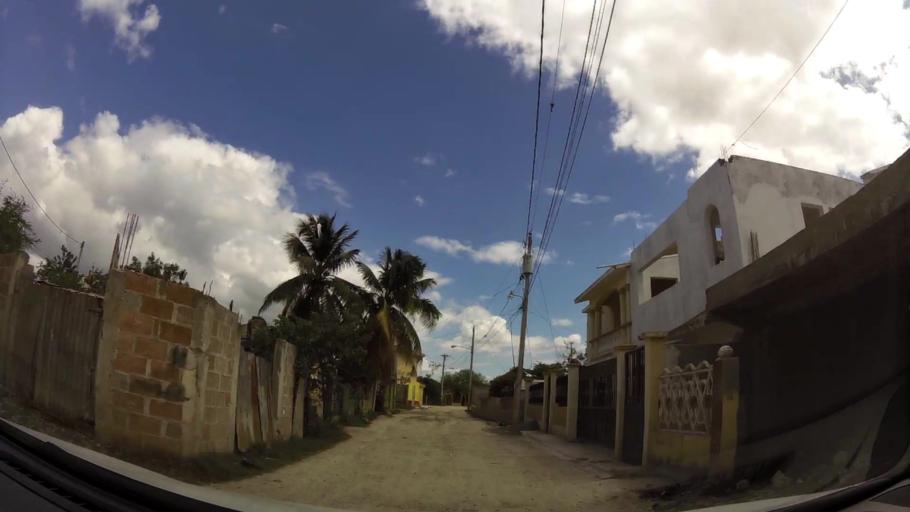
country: DO
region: Santo Domingo
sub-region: Santo Domingo
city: Boca Chica
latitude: 18.4527
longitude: -69.6337
